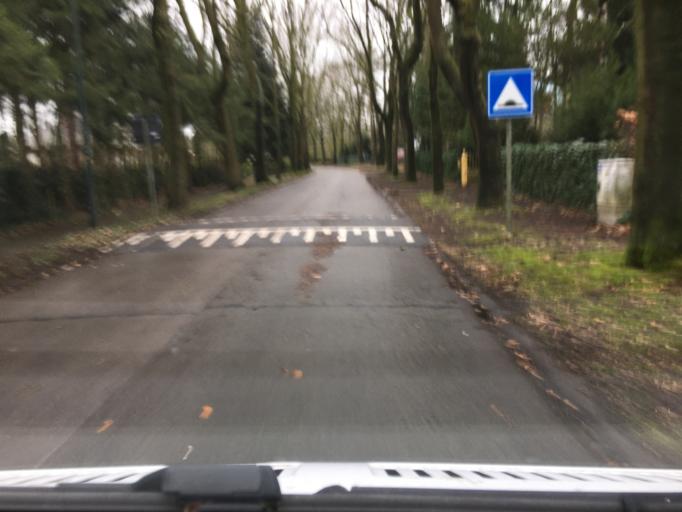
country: BE
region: Flanders
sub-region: Provincie Oost-Vlaanderen
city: Waarschoot
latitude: 51.1808
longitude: 3.6299
